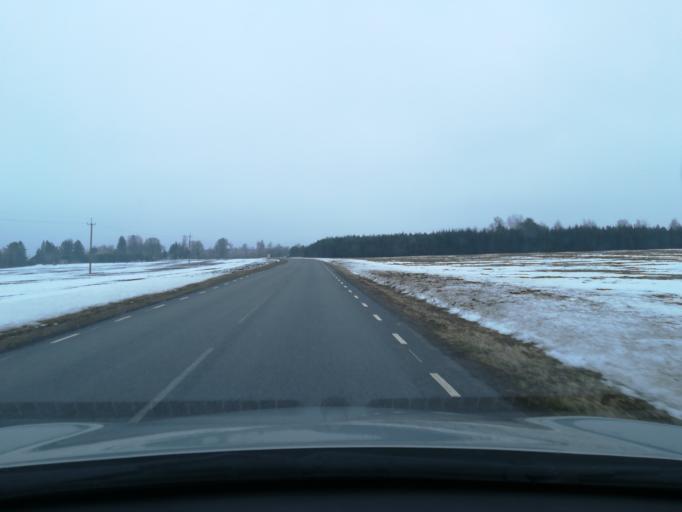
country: EE
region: Harju
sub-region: Kuusalu vald
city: Kuusalu
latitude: 59.4717
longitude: 25.5397
